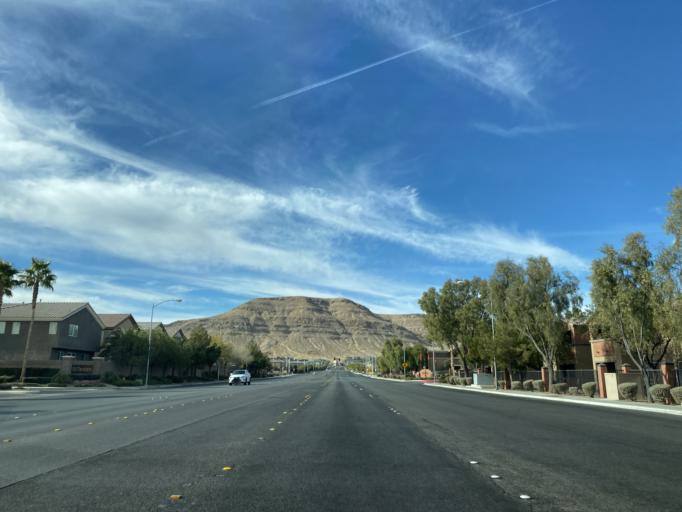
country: US
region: Nevada
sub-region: Clark County
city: Summerlin South
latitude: 36.0702
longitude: -115.3034
